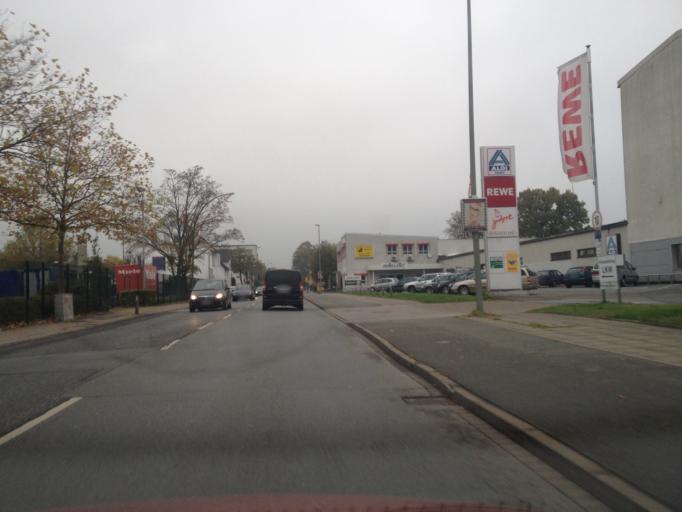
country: DE
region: North Rhine-Westphalia
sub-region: Regierungsbezirk Detmold
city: Bielefeld
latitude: 52.0382
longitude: 8.5436
